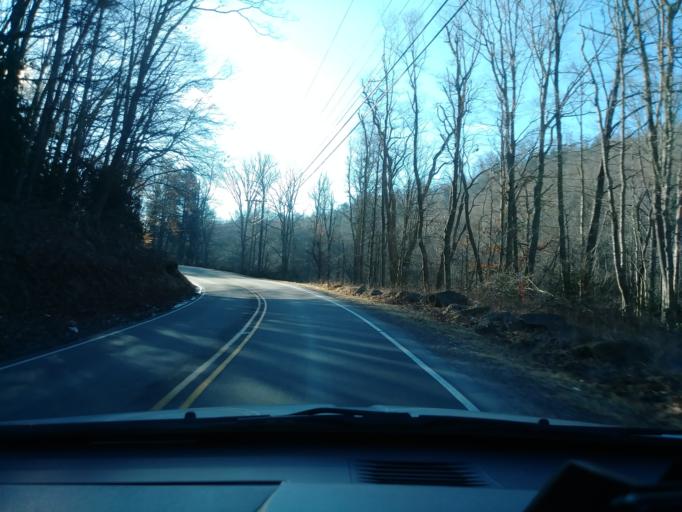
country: US
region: North Carolina
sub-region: Avery County
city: Banner Elk
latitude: 36.1677
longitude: -81.9084
